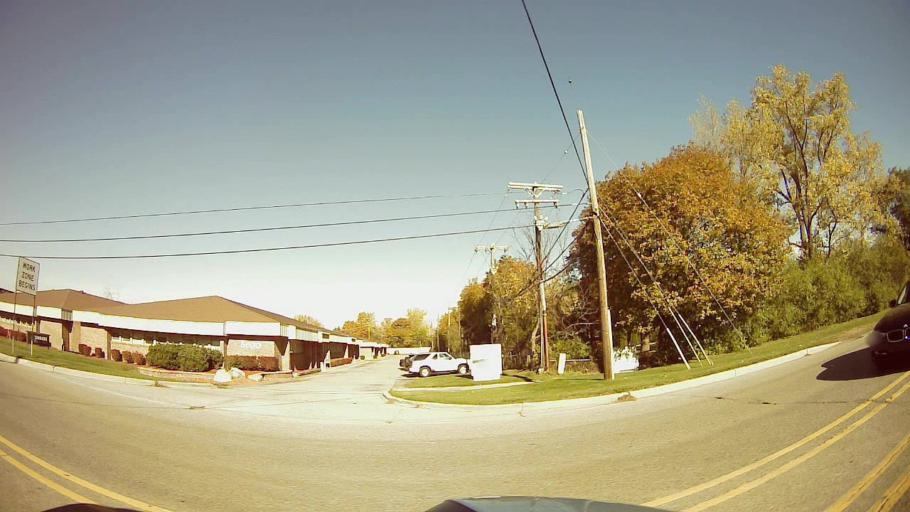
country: US
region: Michigan
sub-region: Oakland County
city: West Bloomfield Township
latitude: 42.5430
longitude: -83.3567
